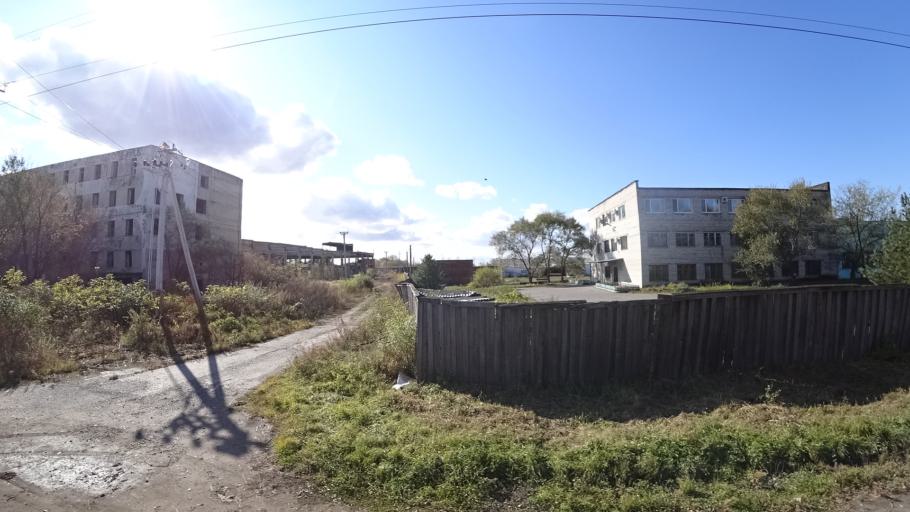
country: RU
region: Khabarovsk Krai
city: Amursk
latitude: 50.0982
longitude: 136.4930
